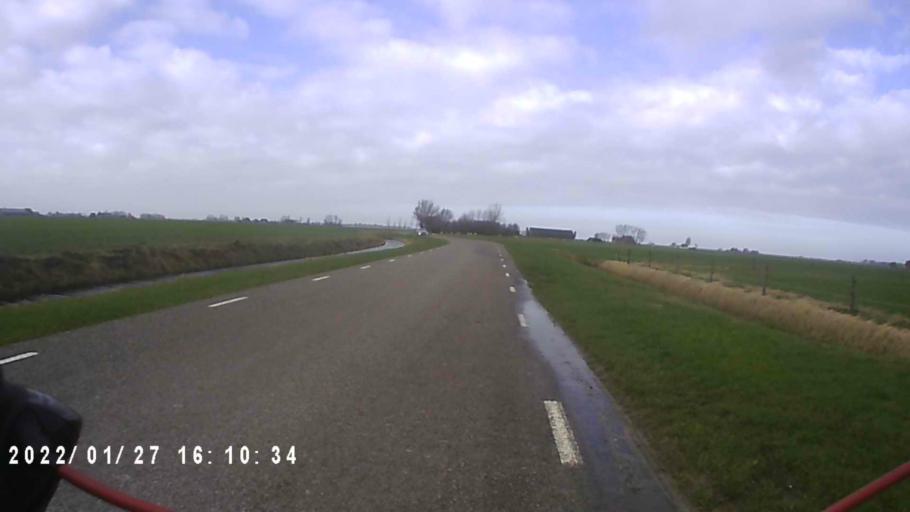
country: NL
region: Friesland
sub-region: Gemeente Dongeradeel
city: Anjum
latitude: 53.3821
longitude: 6.0801
